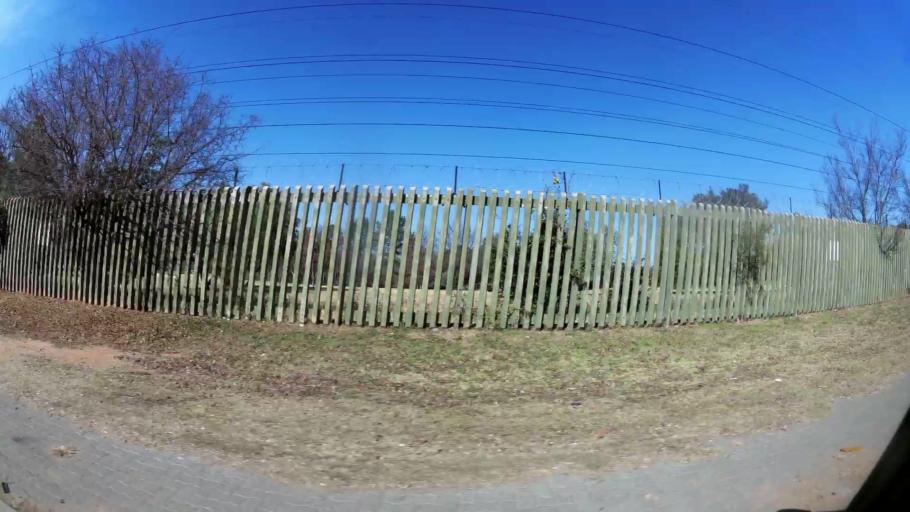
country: ZA
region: Gauteng
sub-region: City of Johannesburg Metropolitan Municipality
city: Roodepoort
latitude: -26.1015
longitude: 27.9644
